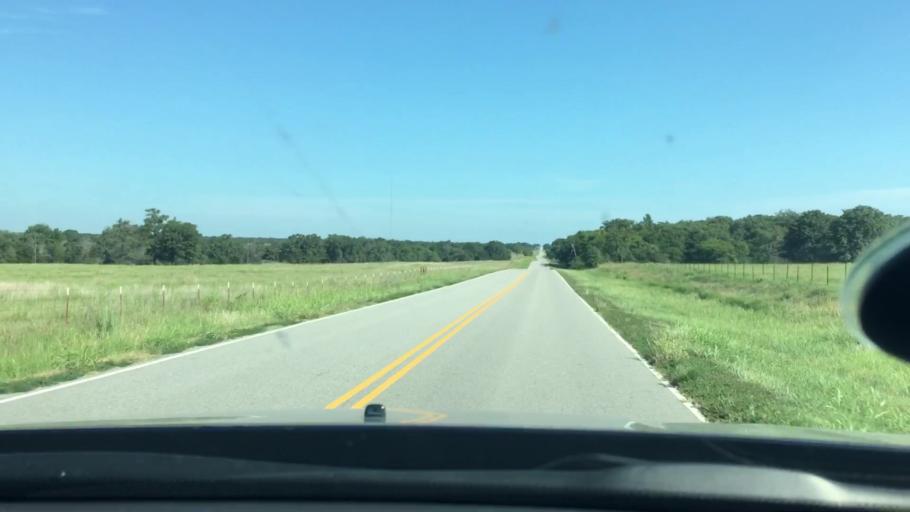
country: US
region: Oklahoma
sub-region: Johnston County
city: Tishomingo
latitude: 34.3077
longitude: -96.5488
